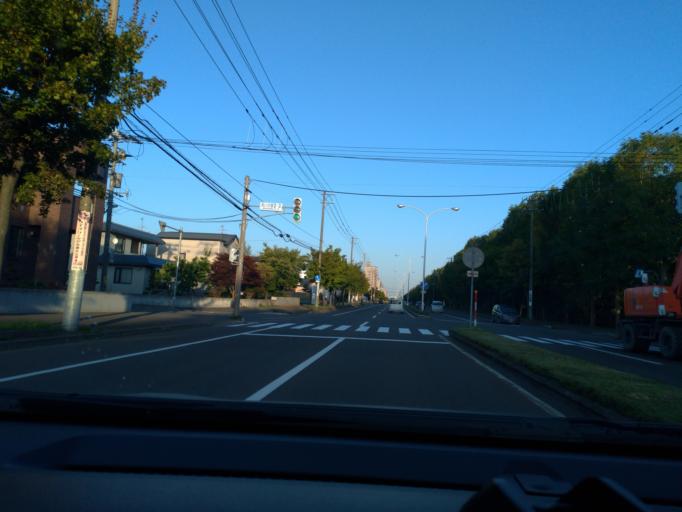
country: JP
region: Hokkaido
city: Ishikari
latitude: 43.1589
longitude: 141.3902
